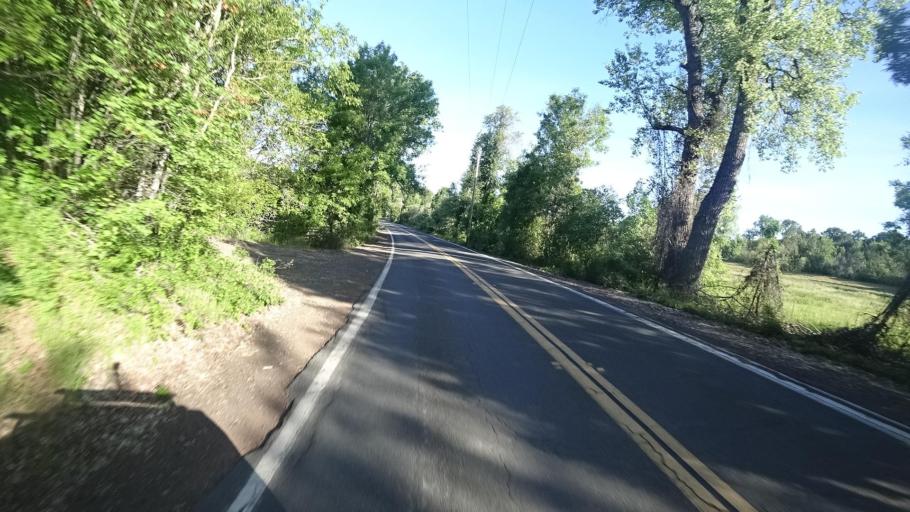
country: US
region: California
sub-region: Lake County
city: North Lakeport
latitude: 39.0937
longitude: -122.9599
